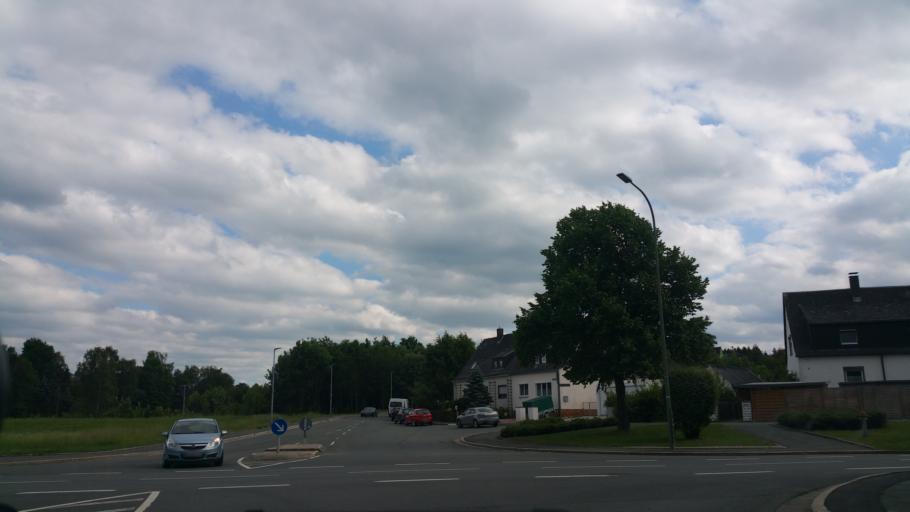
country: DE
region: Bavaria
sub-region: Upper Franconia
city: Rehau
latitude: 50.2398
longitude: 12.0244
